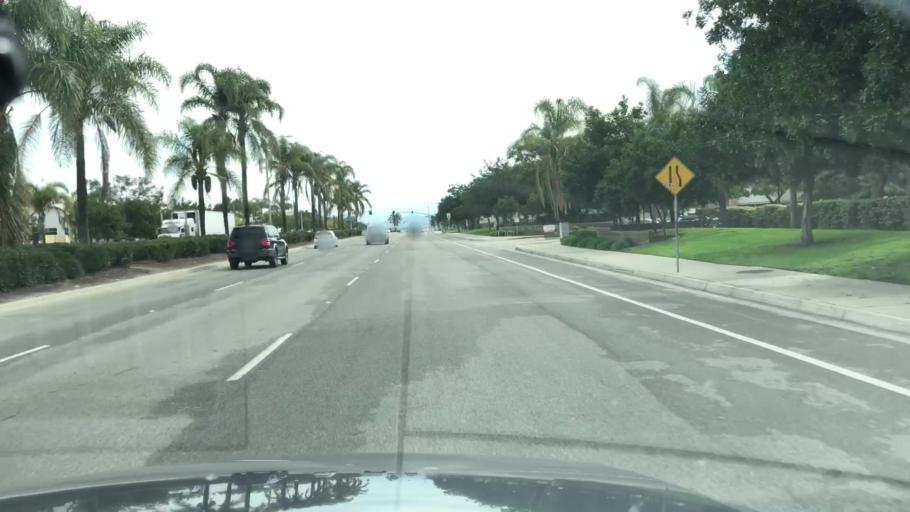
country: US
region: California
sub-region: Ventura County
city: El Rio
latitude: 34.2187
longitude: -119.1480
